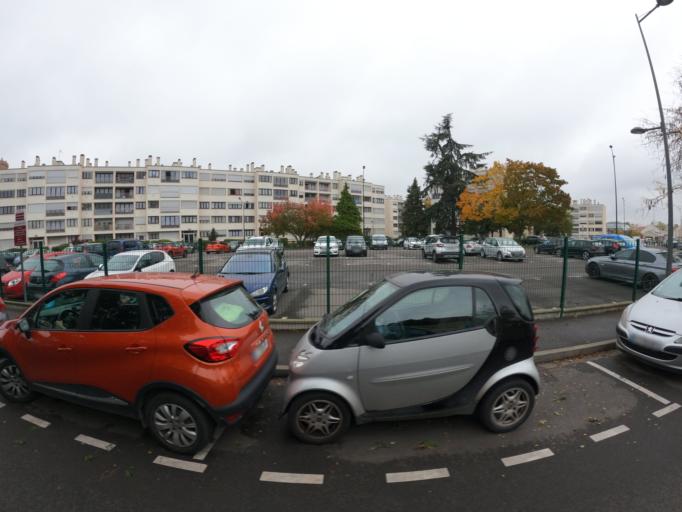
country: FR
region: Ile-de-France
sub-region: Departement du Val-de-Marne
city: Ormesson-sur-Marne
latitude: 48.7861
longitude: 2.5291
